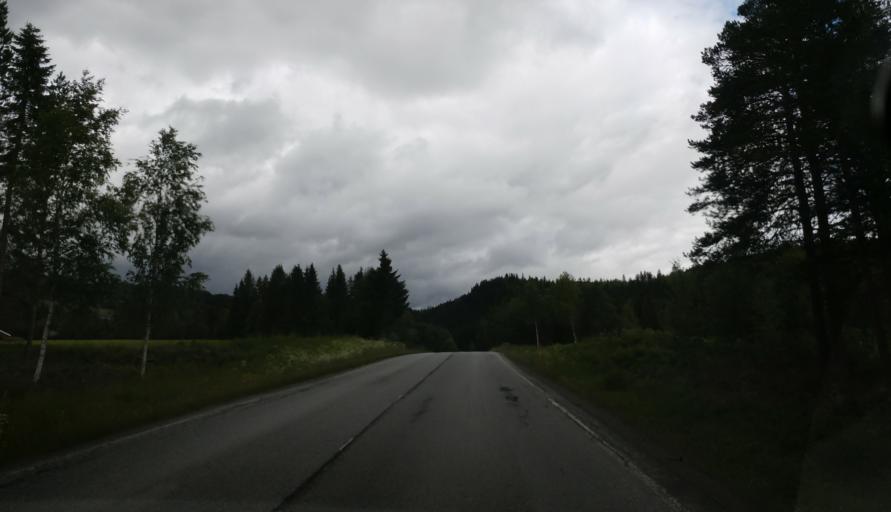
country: NO
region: Sor-Trondelag
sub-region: Selbu
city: Mebonden
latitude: 63.2912
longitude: 11.0737
